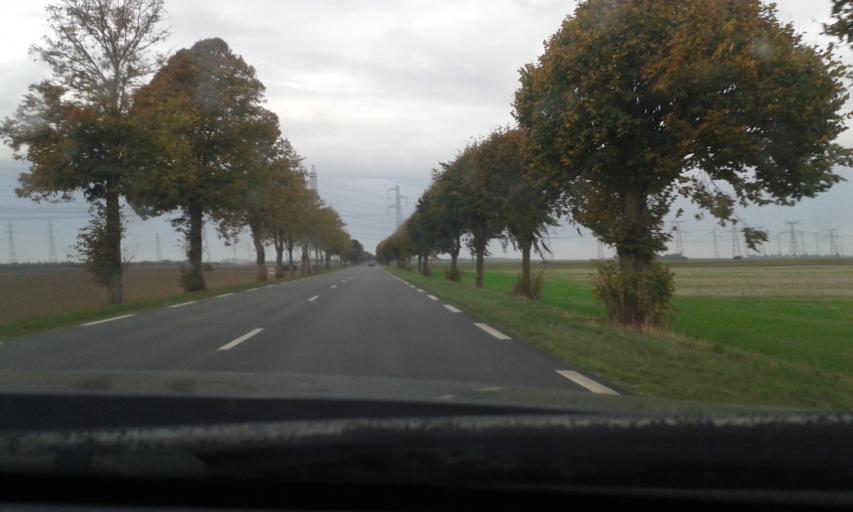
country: FR
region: Centre
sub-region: Departement du Loiret
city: Artenay
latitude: 48.1111
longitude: 1.8620
